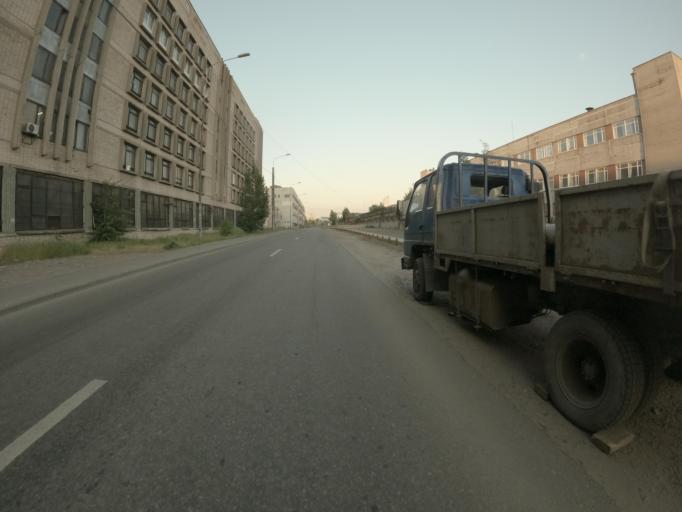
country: RU
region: St.-Petersburg
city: Admiralteisky
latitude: 59.8870
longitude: 30.2859
